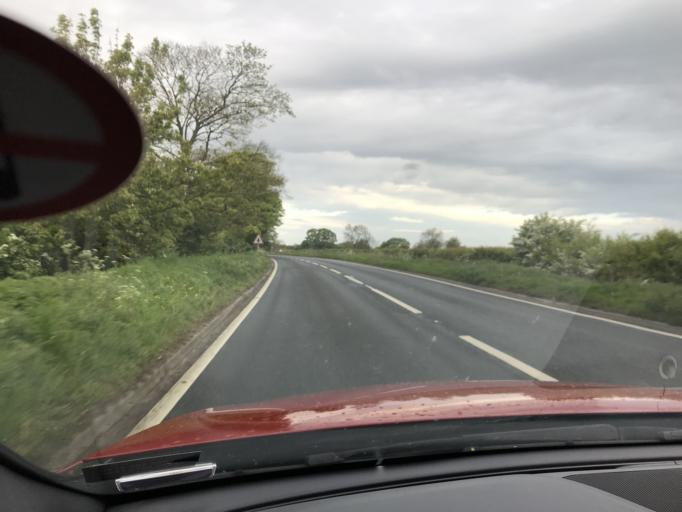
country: GB
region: England
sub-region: East Riding of Yorkshire
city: Cherry Burton
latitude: 53.8447
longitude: -0.4880
